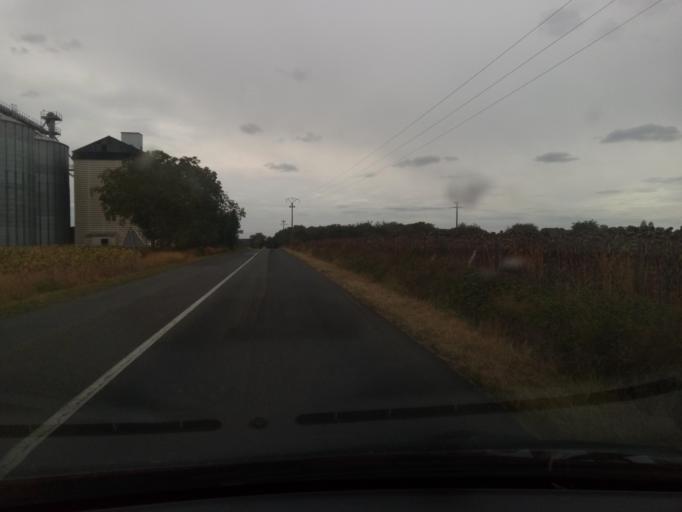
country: FR
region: Centre
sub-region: Departement d'Indre-et-Loire
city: Yzeures-sur-Creuse
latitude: 46.6816
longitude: 0.8591
